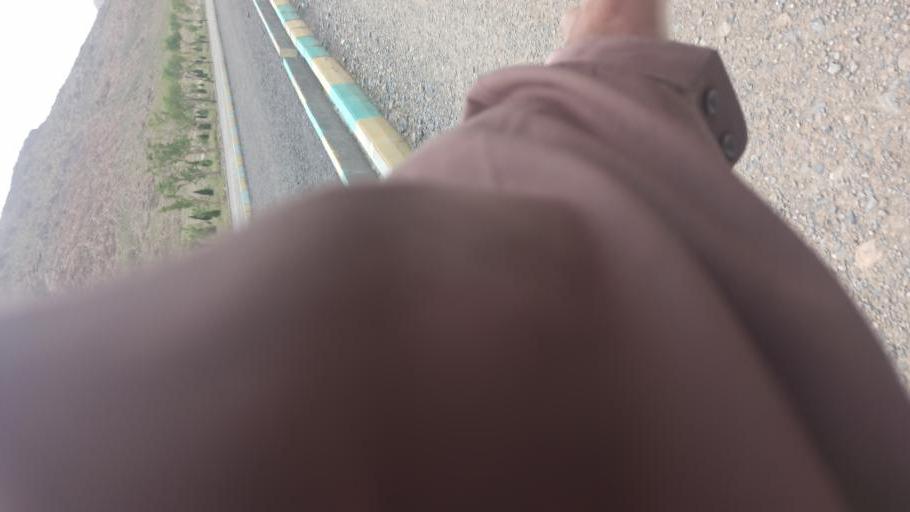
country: IR
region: Markazi
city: Arak
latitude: 34.0542
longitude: 49.6870
